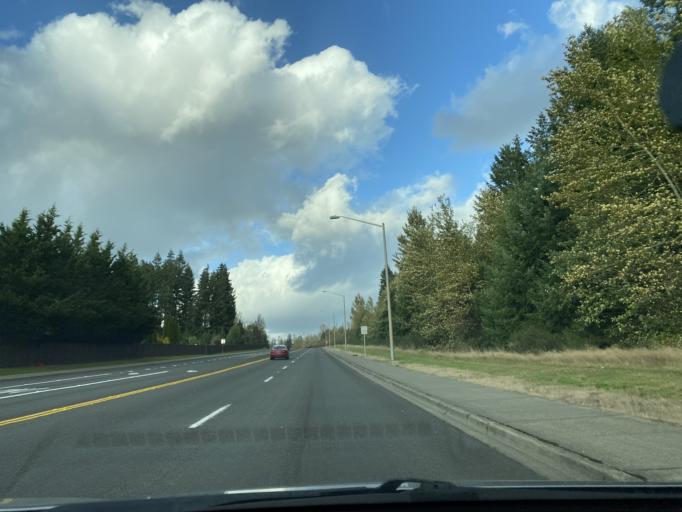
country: US
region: Washington
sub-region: Pierce County
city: Graham
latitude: 47.0915
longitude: -122.2679
